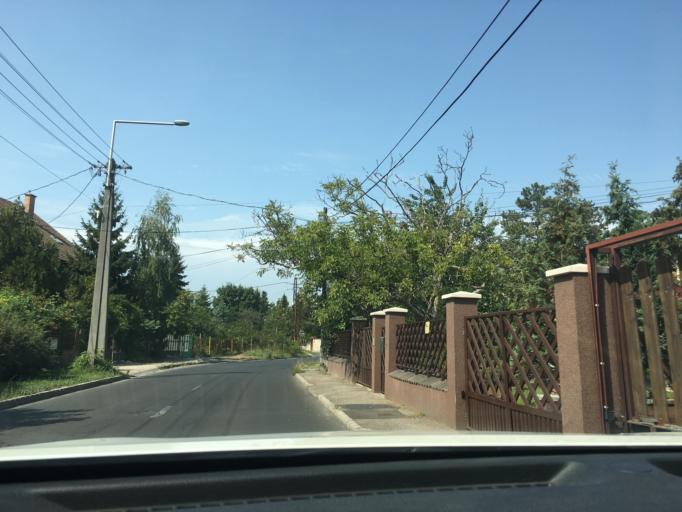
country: HU
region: Budapest
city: Budapest XVII. keruelet
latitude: 47.4927
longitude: 19.2551
